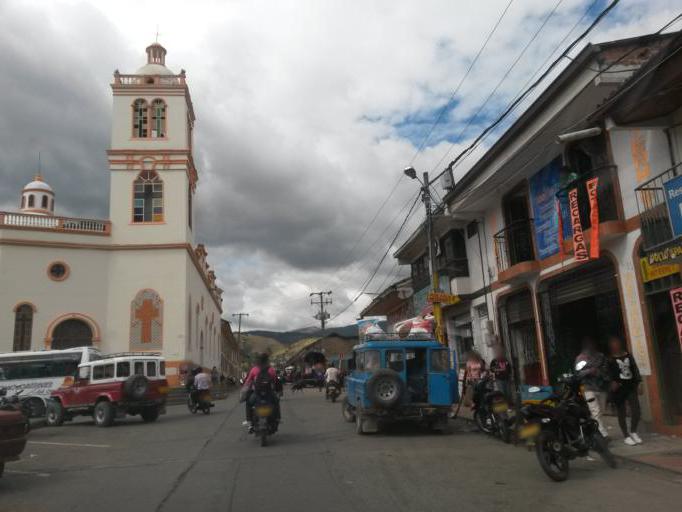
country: CO
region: Cauca
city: Silvia
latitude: 2.6109
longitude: -76.3789
